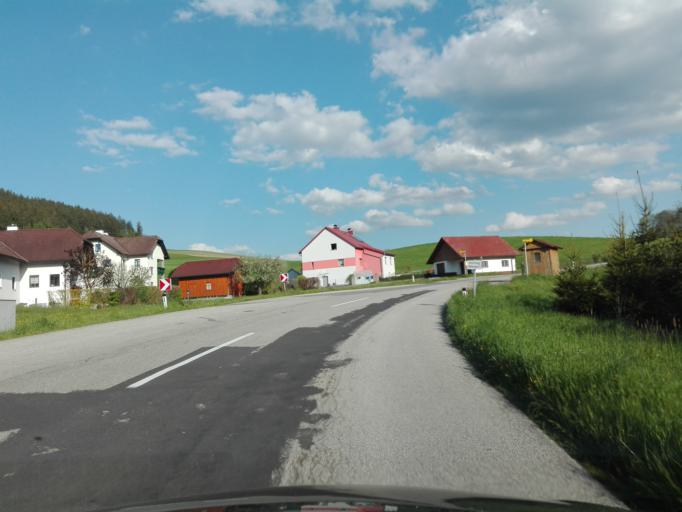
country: AT
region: Upper Austria
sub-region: Politischer Bezirk Rohrbach
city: Atzesberg
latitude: 48.4776
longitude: 13.9400
